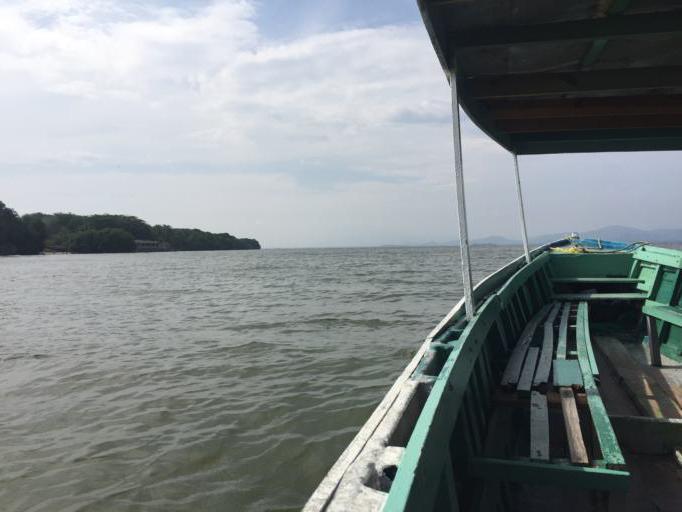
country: MX
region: Guerrero
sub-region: Coyuca de Benitez
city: Colonia Luces en el Mar
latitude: 16.9099
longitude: -99.9754
